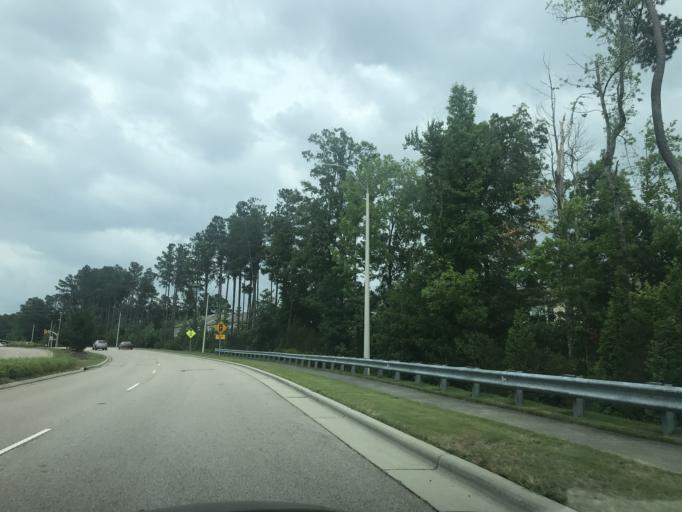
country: US
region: North Carolina
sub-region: Wake County
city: Morrisville
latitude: 35.8141
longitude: -78.8504
